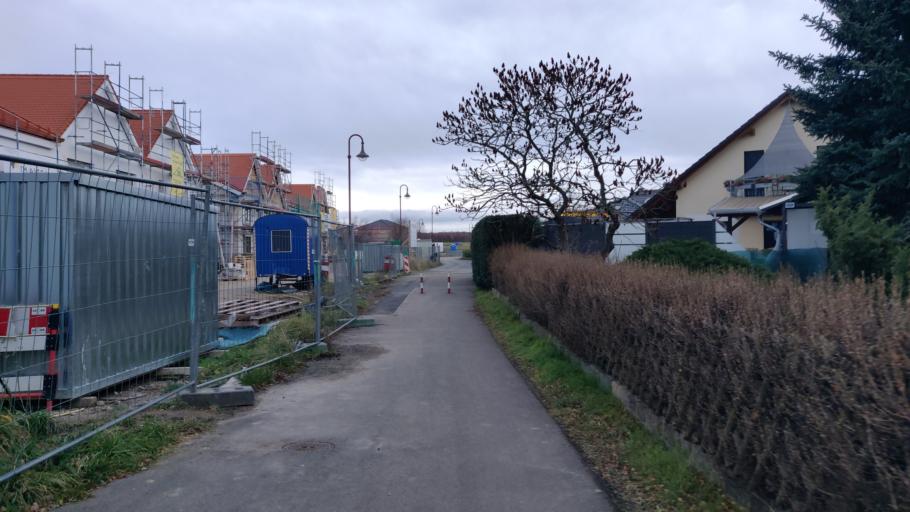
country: DE
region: Saxony
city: Bad Lausick
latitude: 51.1526
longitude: 12.6515
